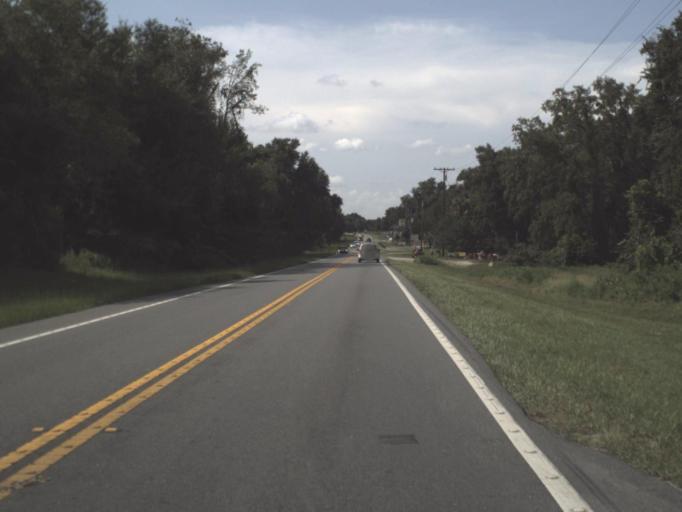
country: US
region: Florida
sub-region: Citrus County
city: Hernando
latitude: 28.8836
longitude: -82.3654
